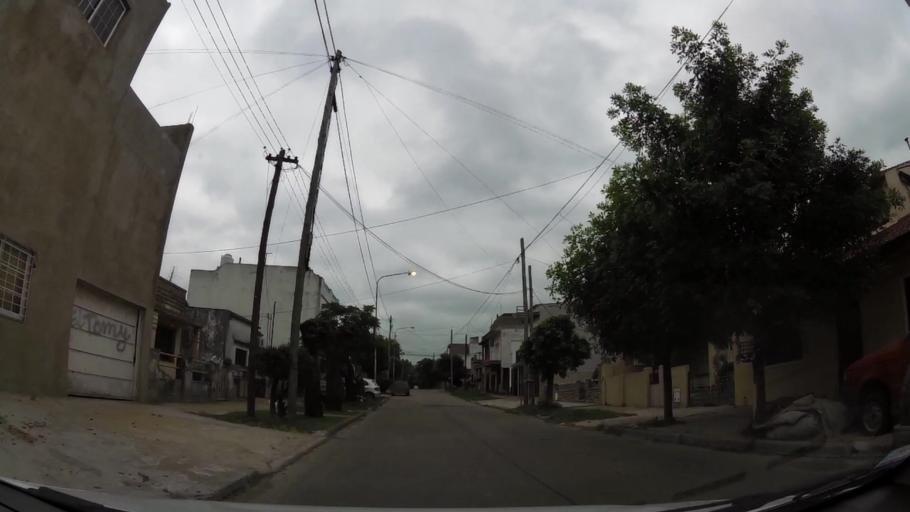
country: AR
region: Buenos Aires F.D.
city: Villa Lugano
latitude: -34.7124
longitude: -58.5170
